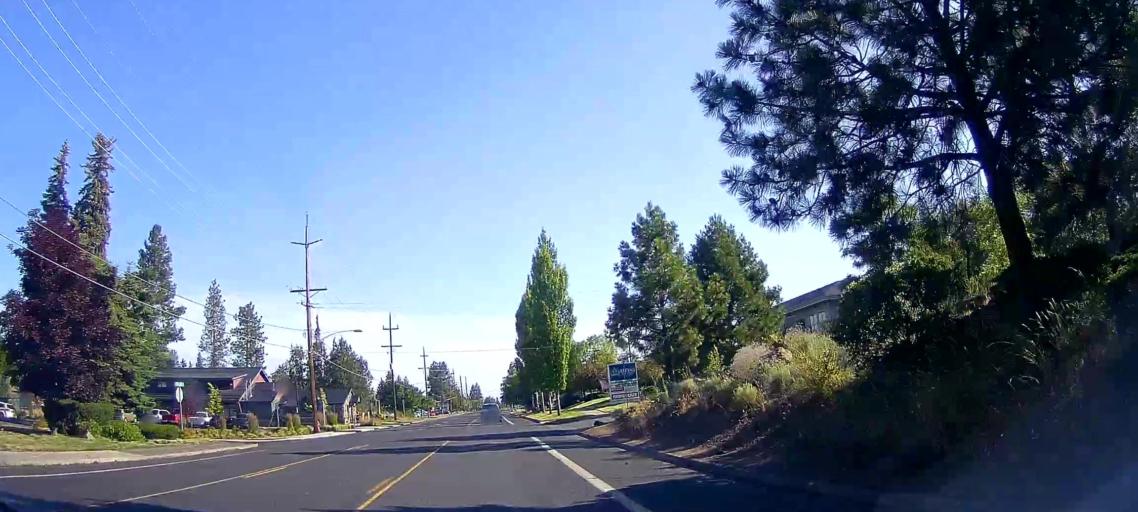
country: US
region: Oregon
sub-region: Deschutes County
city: Bend
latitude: 44.0713
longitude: -121.3058
